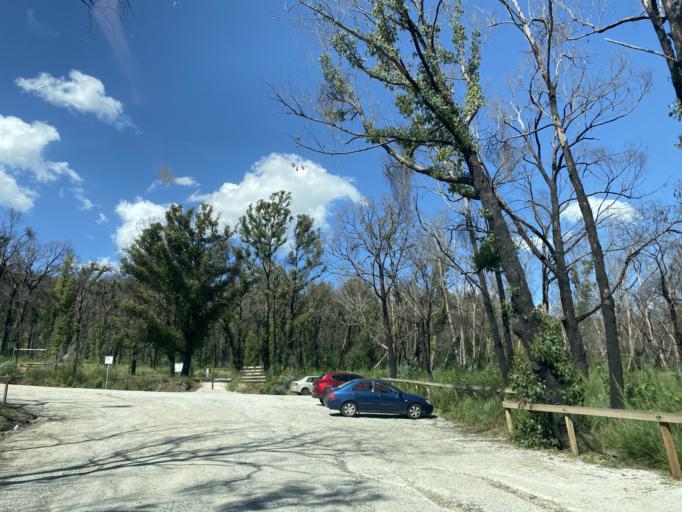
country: AU
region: Victoria
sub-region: Cardinia
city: Garfield
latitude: -38.0521
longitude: 145.6767
